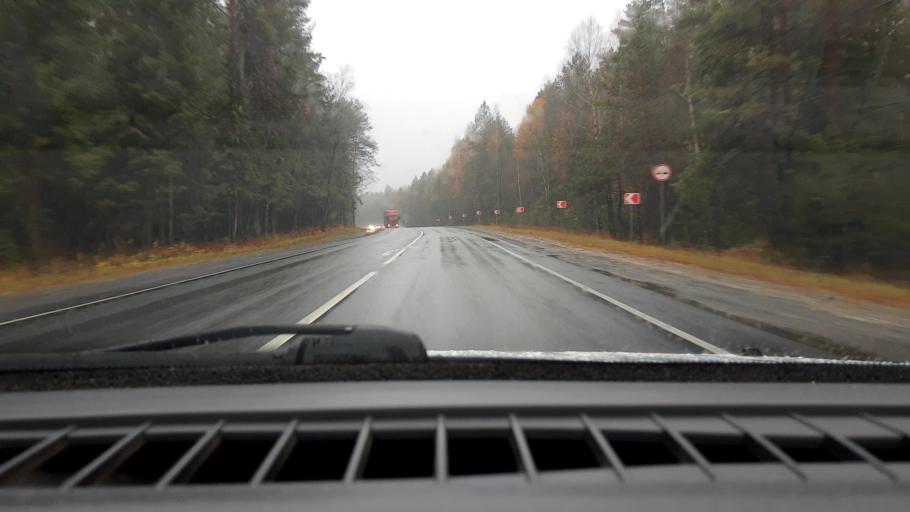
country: RU
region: Nizjnij Novgorod
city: Linda
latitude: 56.6817
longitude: 44.1583
